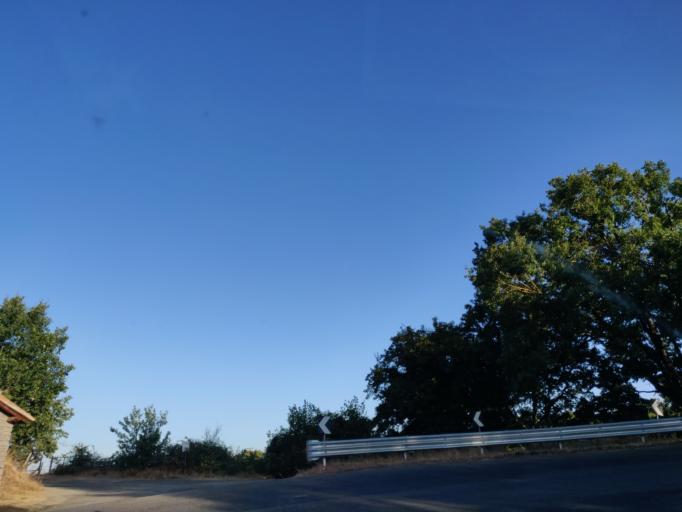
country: IT
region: Latium
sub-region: Provincia di Viterbo
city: Latera
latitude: 42.6392
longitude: 11.8391
